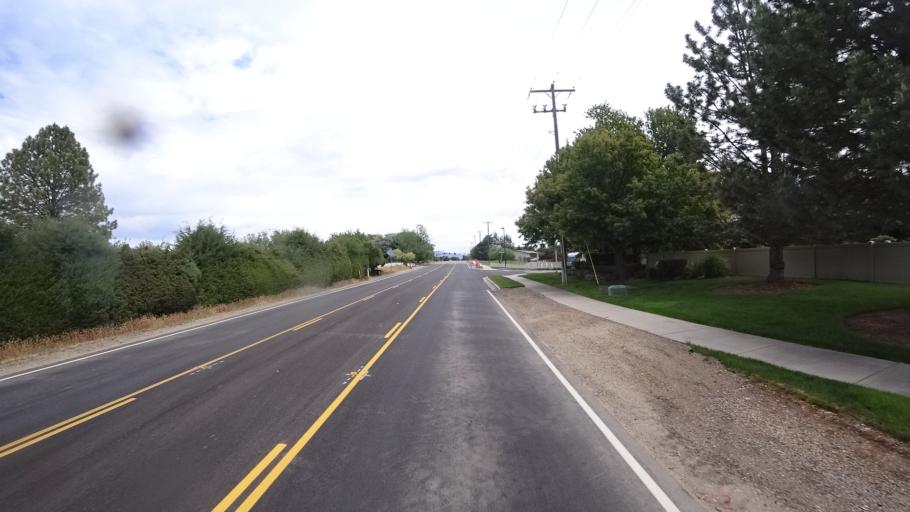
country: US
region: Idaho
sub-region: Ada County
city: Meridian
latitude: 43.5757
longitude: -116.3577
